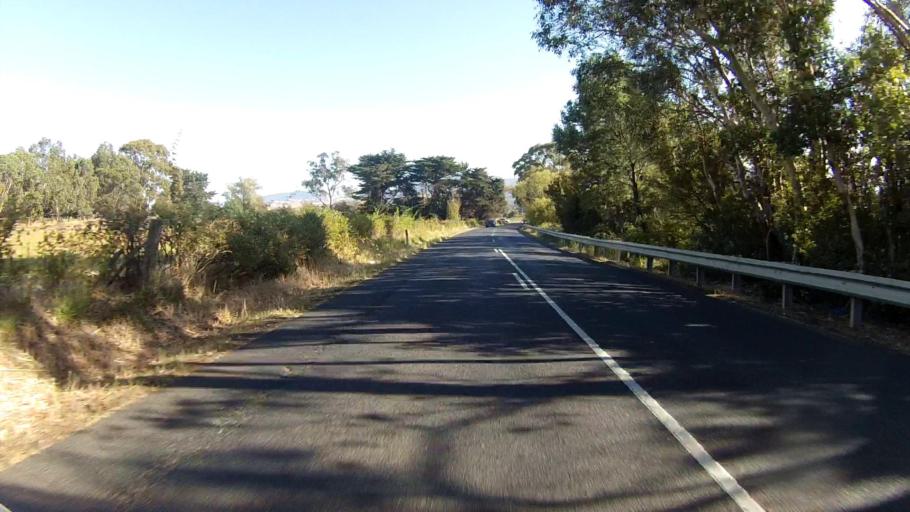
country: AU
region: Tasmania
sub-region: Derwent Valley
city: New Norfolk
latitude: -42.7751
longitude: 147.0279
